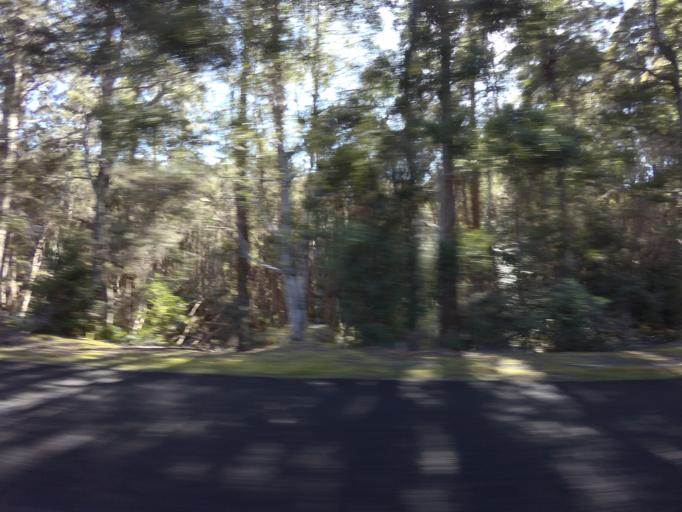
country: AU
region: Tasmania
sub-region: Derwent Valley
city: New Norfolk
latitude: -42.7549
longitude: 146.5259
